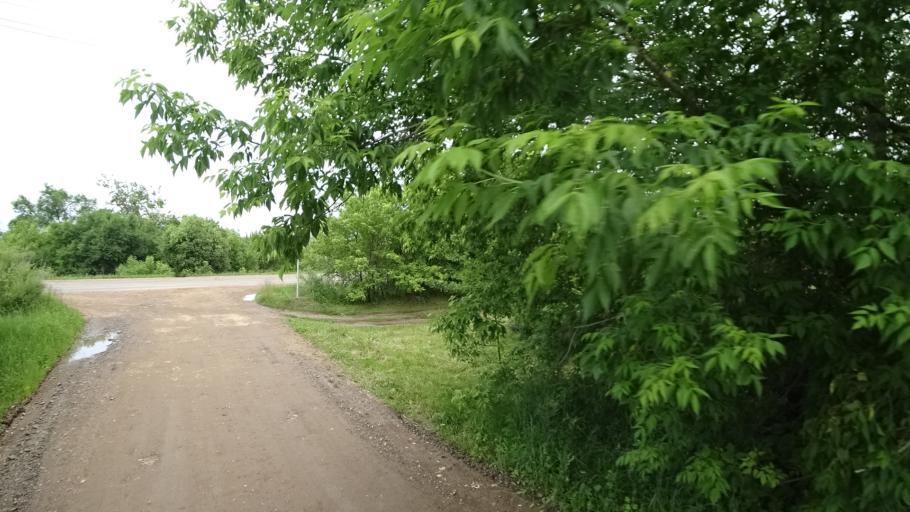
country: RU
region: Primorskiy
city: Novosysoyevka
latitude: 44.2300
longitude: 133.3665
